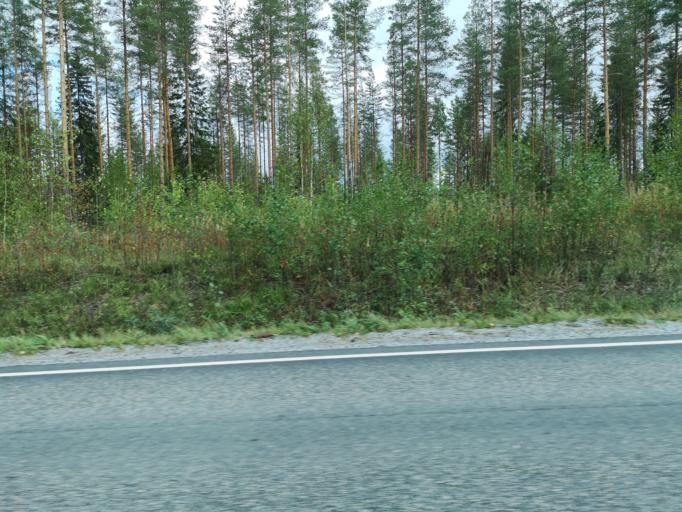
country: FI
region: Central Finland
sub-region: Jyvaeskylae
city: Hankasalmi
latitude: 62.3528
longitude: 26.4580
